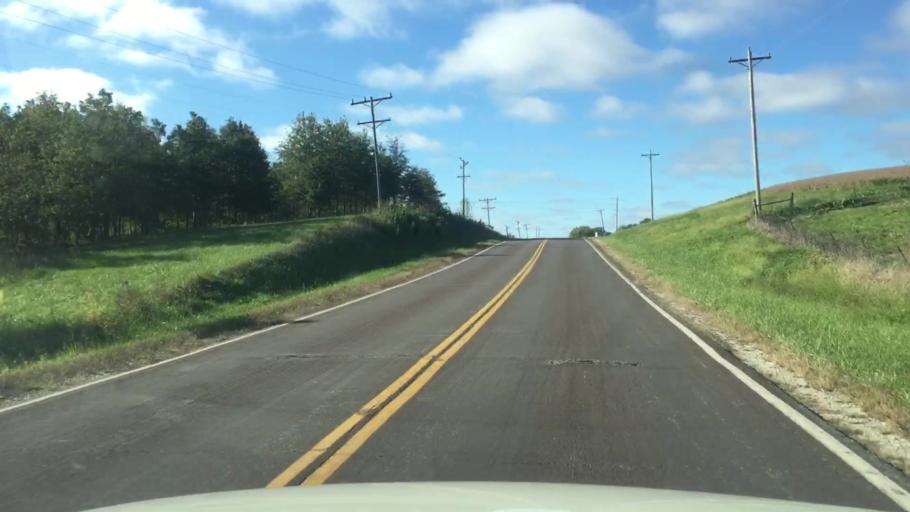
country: US
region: Missouri
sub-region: Howard County
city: Fayette
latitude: 39.1076
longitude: -92.7322
